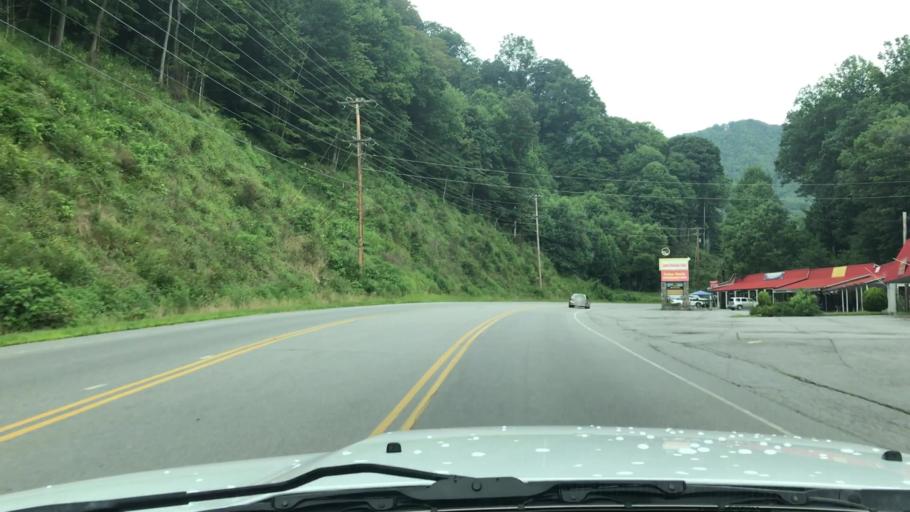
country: US
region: North Carolina
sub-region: Haywood County
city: Maggie Valley
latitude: 35.5216
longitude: -83.1102
